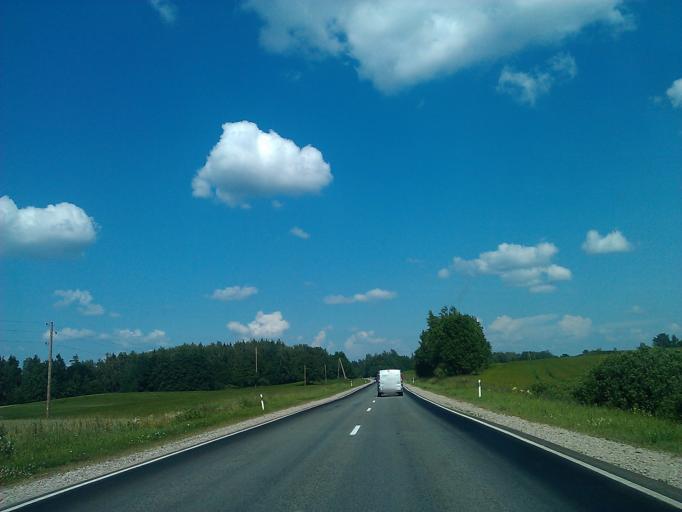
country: LV
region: Vainode
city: Vainode
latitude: 56.6179
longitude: 21.8018
